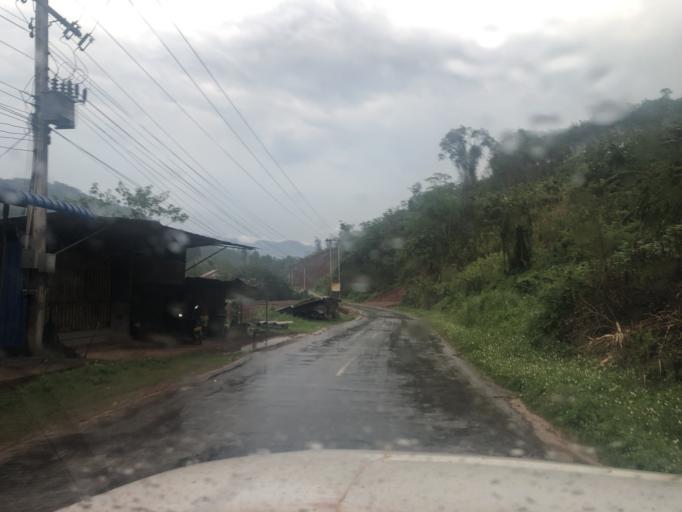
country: LA
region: Phongsali
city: Phongsali
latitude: 21.4026
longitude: 101.9658
